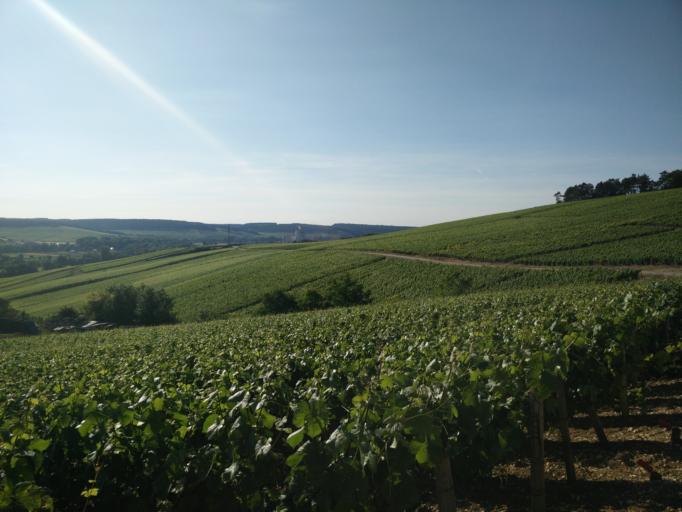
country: FR
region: Champagne-Ardenne
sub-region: Departement de l'Aube
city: Bar-sur-Seine
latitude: 48.0560
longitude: 4.4068
